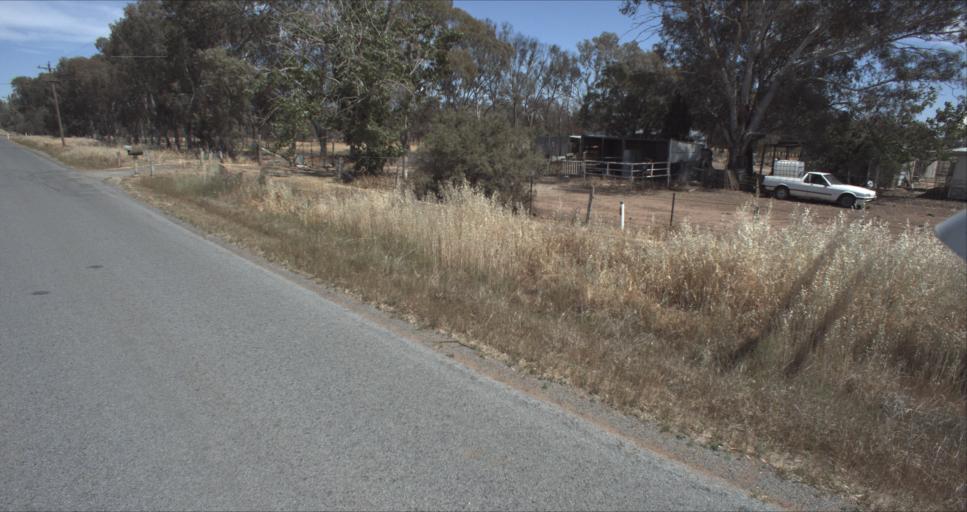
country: AU
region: New South Wales
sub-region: Leeton
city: Leeton
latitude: -34.5794
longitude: 146.4287
